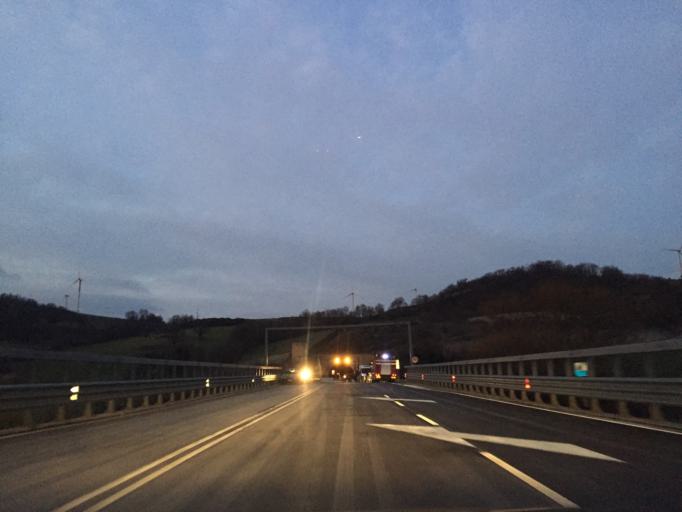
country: IT
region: Apulia
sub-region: Provincia di Foggia
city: Volturino
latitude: 41.4669
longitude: 15.0943
